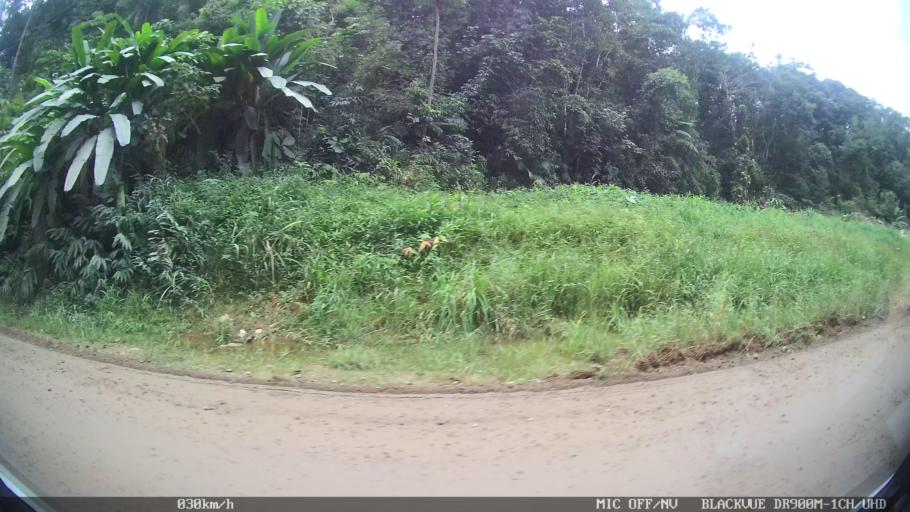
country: BR
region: Santa Catarina
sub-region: Joinville
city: Joinville
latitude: -26.2477
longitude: -48.9249
